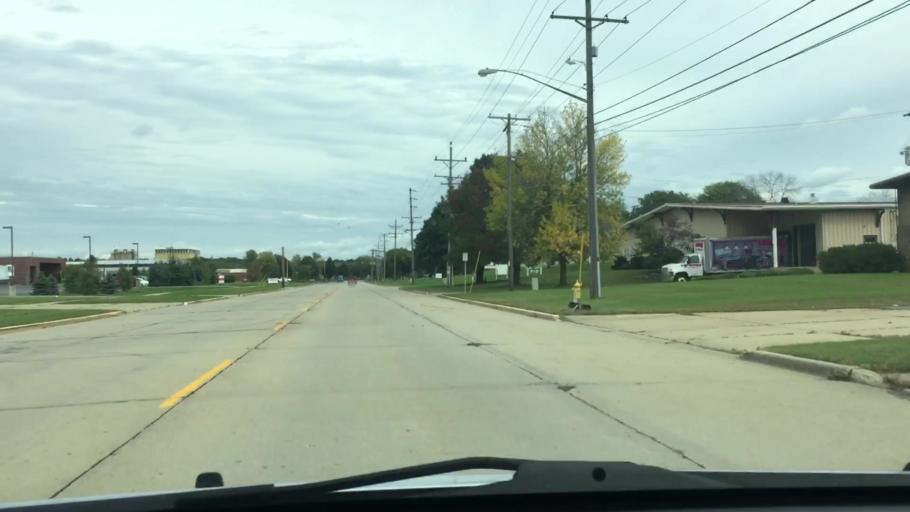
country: US
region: Wisconsin
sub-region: Waukesha County
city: Waukesha
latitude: 42.9902
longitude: -88.2498
